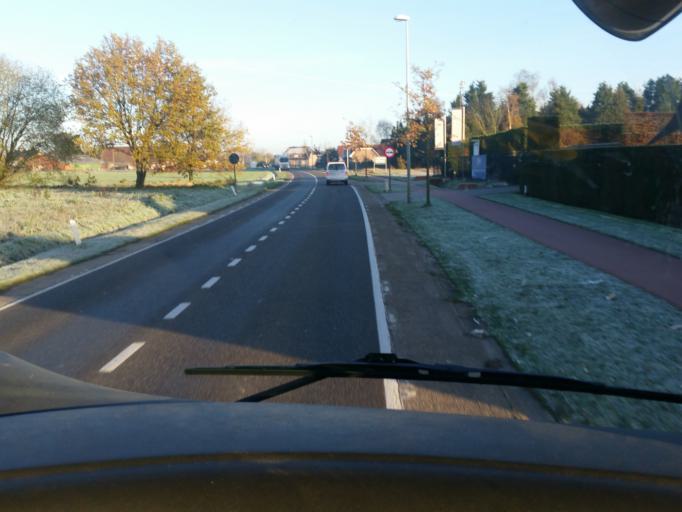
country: BE
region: Flanders
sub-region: Provincie Antwerpen
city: Arendonk
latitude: 51.3045
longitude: 5.0948
